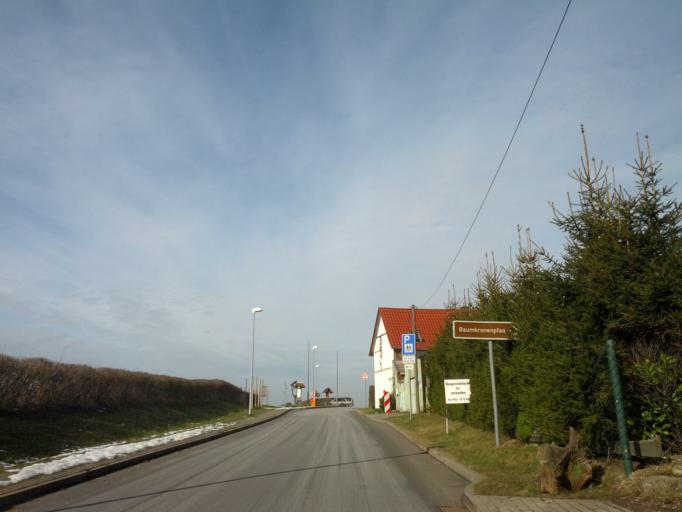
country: DE
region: Thuringia
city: Weberstedt
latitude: 51.0653
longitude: 10.4916
